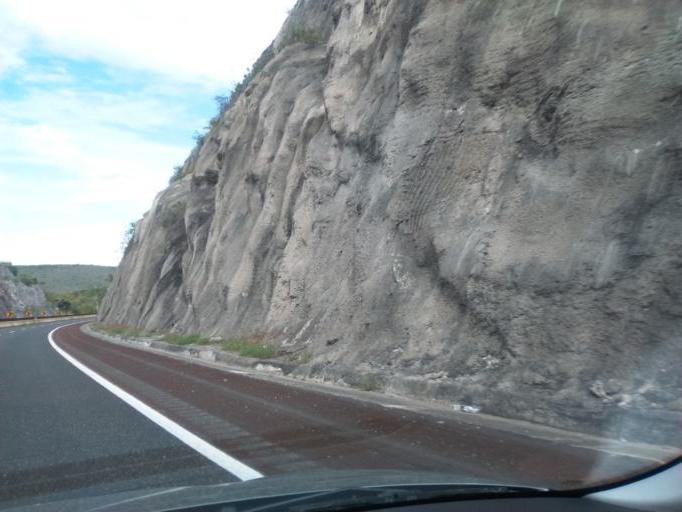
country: MX
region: Guerrero
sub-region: Eduardo Neri
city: Tlanipatla
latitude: 17.8379
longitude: -99.4488
